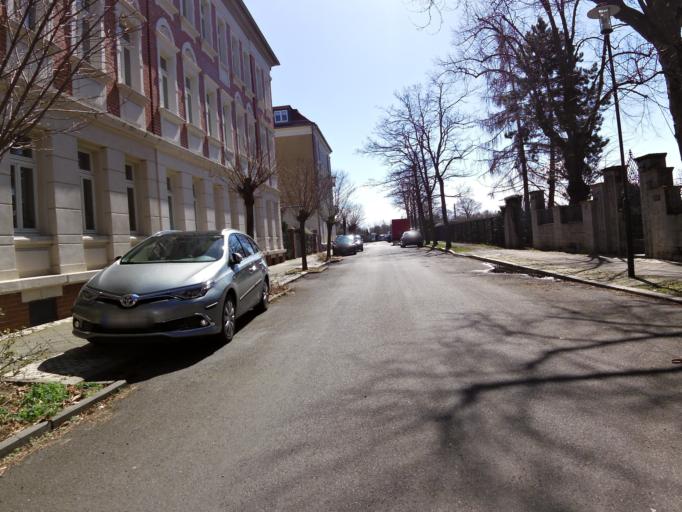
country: DE
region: Saxony
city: Markkleeberg
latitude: 51.2764
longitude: 12.3749
